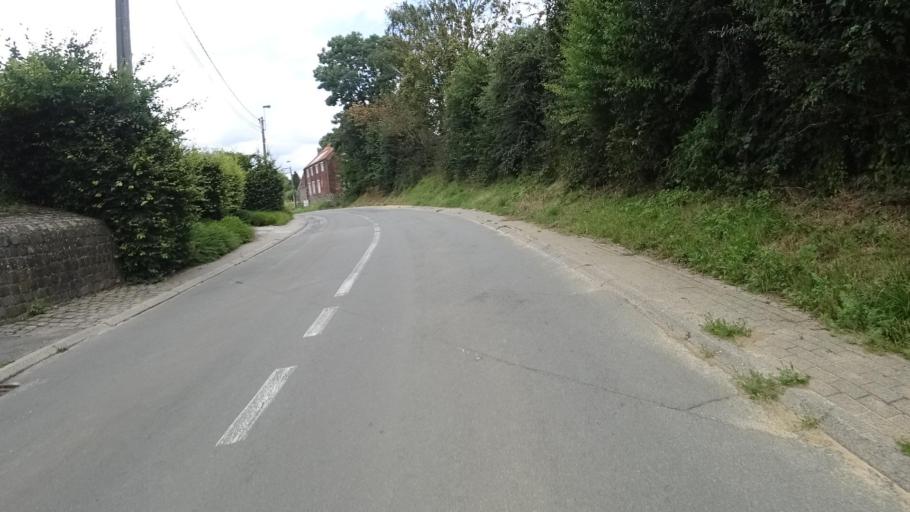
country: BE
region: Wallonia
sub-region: Province du Brabant Wallon
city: Chastre
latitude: 50.5837
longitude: 4.6110
